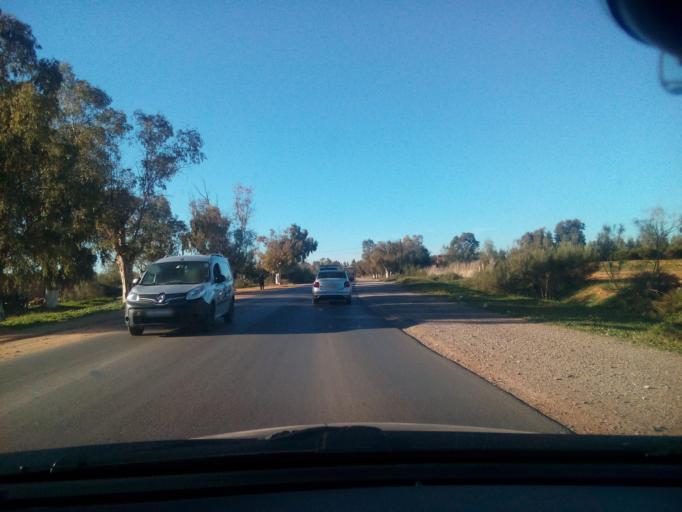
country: DZ
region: Mostaganem
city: Mostaganem
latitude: 35.9020
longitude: 0.2130
